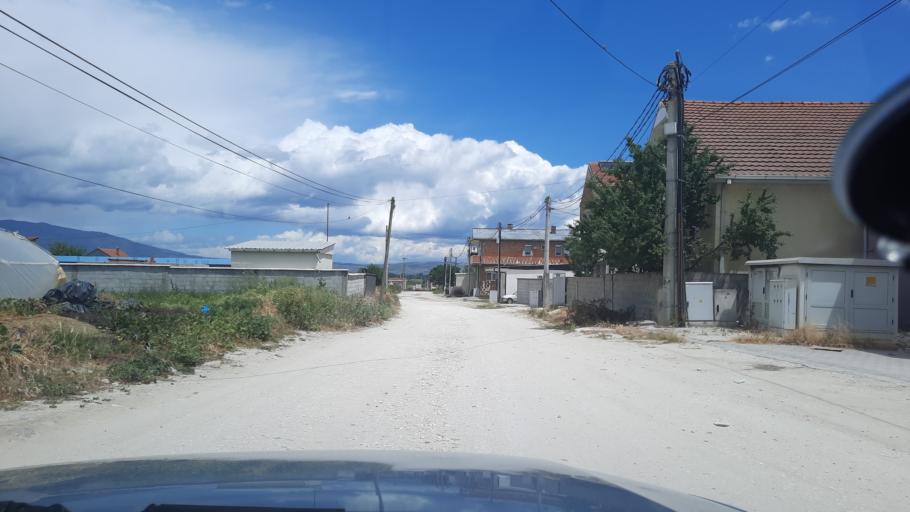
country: MK
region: Studenicani
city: Studenichani
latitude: 41.9257
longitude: 21.5397
